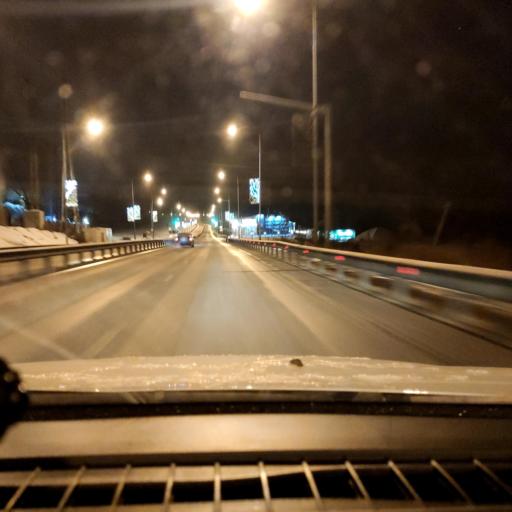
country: RU
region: Samara
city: Volzhskiy
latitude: 53.3790
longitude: 50.1696
